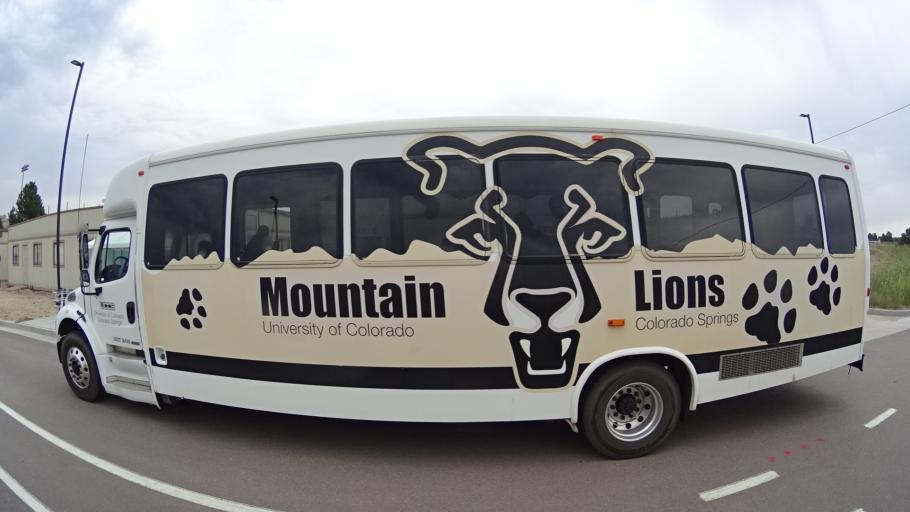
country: US
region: Colorado
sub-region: El Paso County
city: Colorado Springs
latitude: 38.9024
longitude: -104.8146
